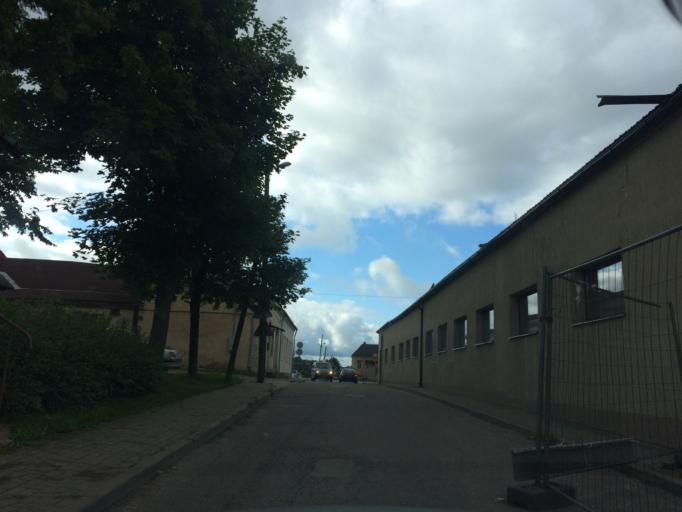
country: LV
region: Rezekne
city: Rezekne
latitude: 56.5002
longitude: 27.3348
